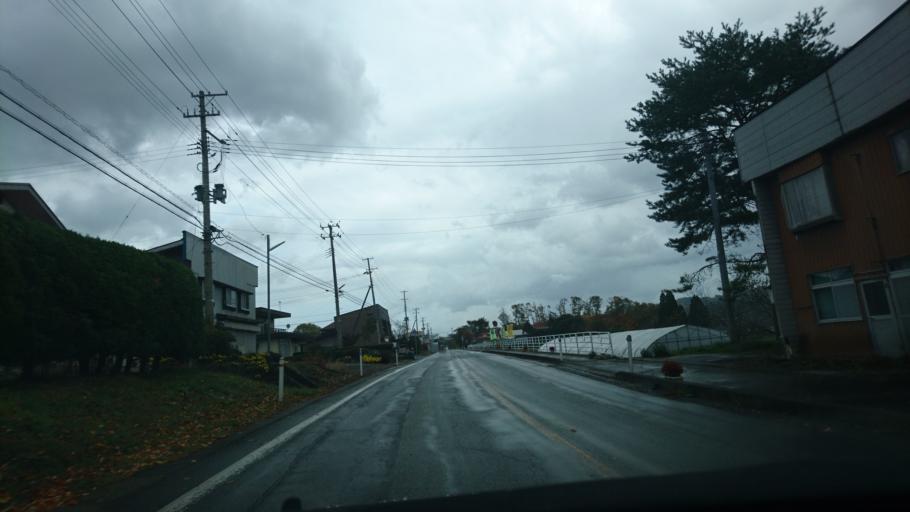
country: JP
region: Iwate
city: Shizukuishi
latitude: 39.6719
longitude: 140.9838
